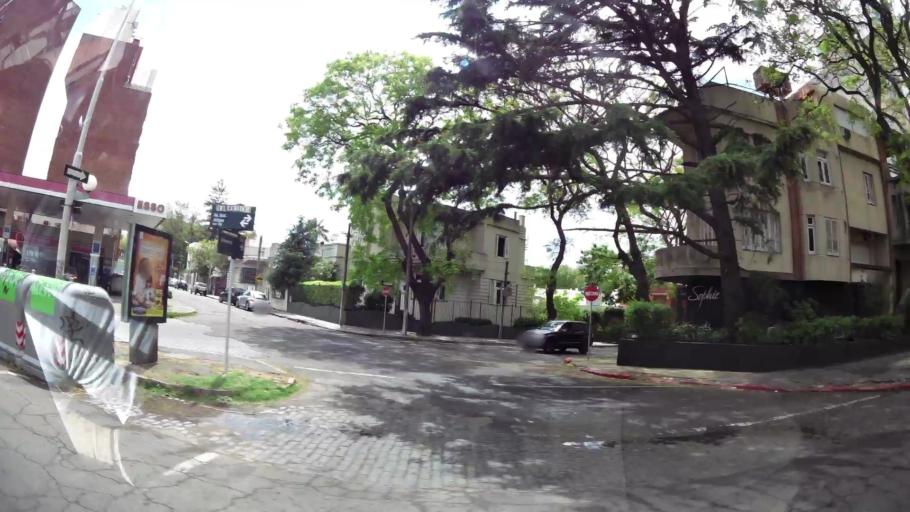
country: UY
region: Montevideo
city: Montevideo
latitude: -34.9173
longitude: -56.1624
